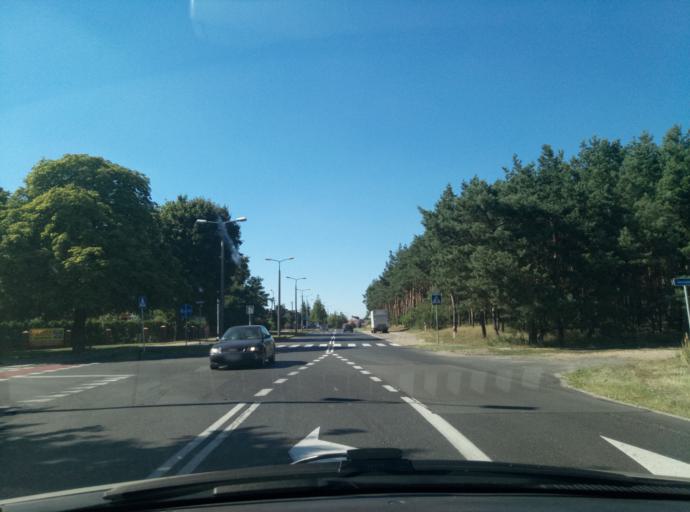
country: PL
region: Kujawsko-Pomorskie
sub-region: Torun
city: Torun
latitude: 53.0443
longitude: 18.5947
